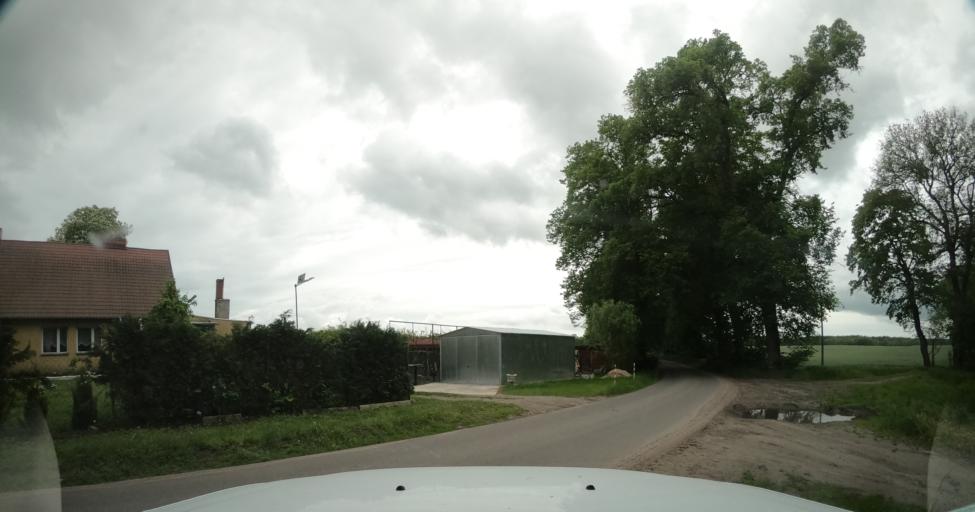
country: PL
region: West Pomeranian Voivodeship
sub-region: Powiat stargardzki
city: Suchan
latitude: 53.2518
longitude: 15.2561
